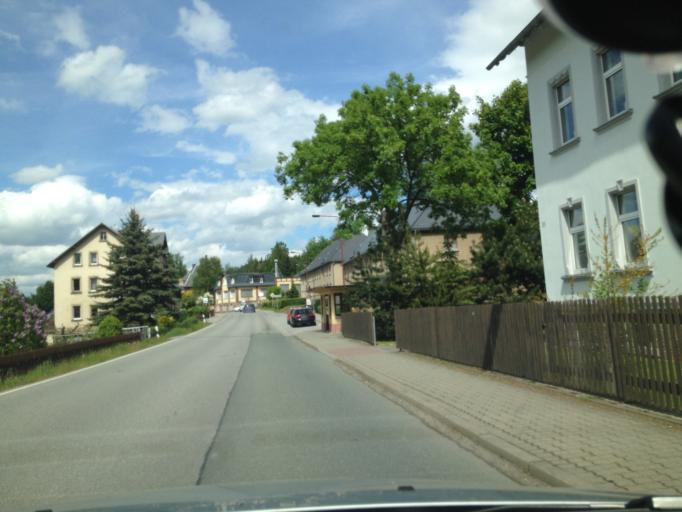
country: DE
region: Saxony
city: Barenstein
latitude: 50.5195
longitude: 12.9953
